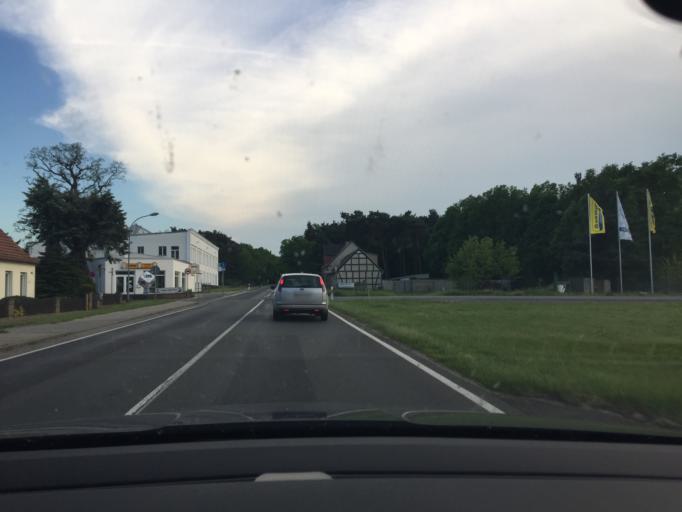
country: DE
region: Brandenburg
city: Treuenbrietzen
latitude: 52.0830
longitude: 12.8422
